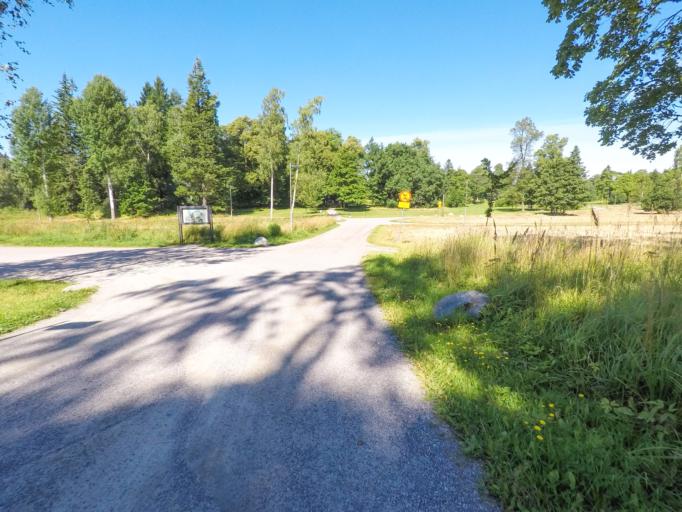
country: FI
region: Uusimaa
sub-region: Helsinki
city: Helsinki
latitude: 60.1778
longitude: 25.0334
